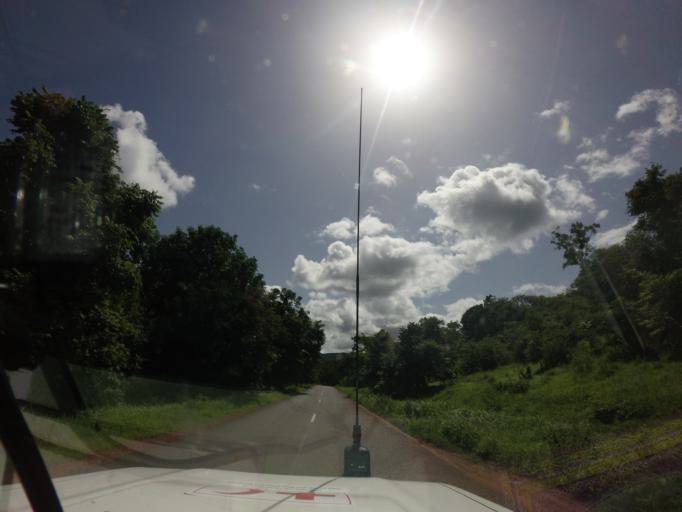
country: GN
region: Mamou
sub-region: Mamou Prefecture
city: Mamou
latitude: 10.2702
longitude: -11.9016
